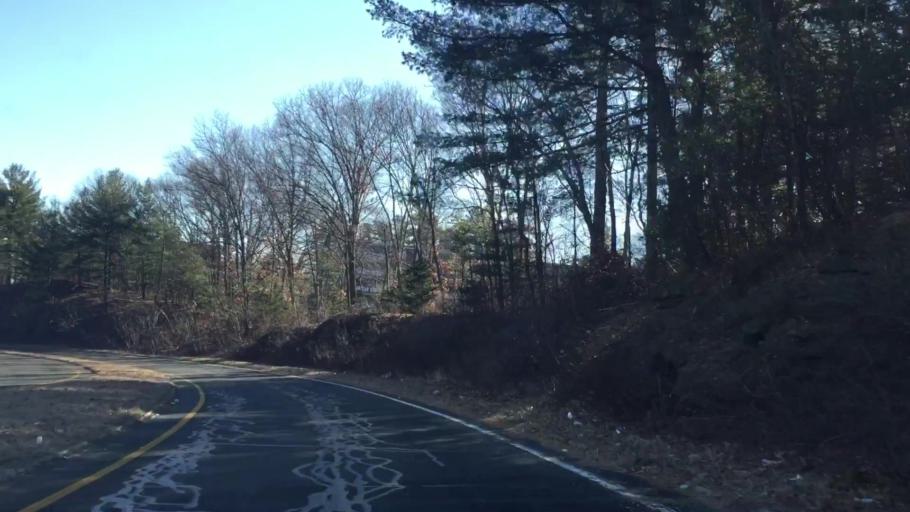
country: US
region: Massachusetts
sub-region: Middlesex County
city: Stoneham
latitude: 42.5018
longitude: -71.1050
